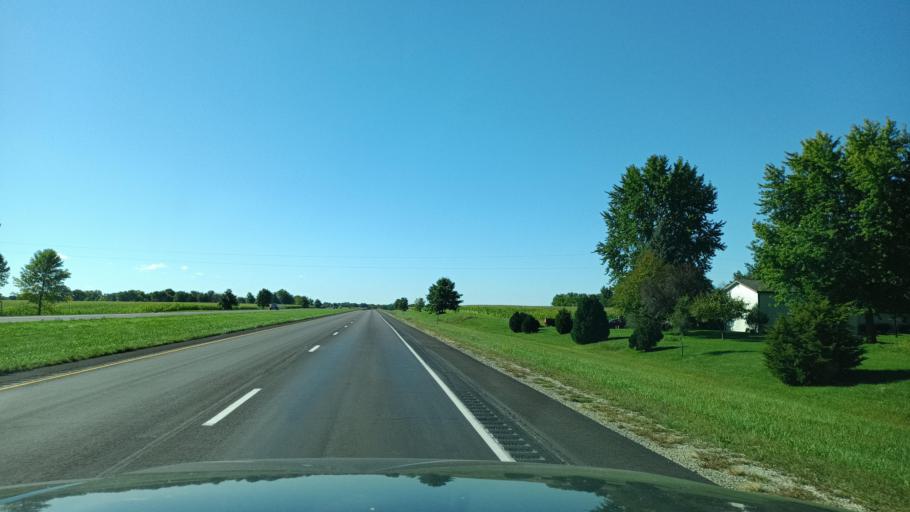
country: US
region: Iowa
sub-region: Lee County
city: Keokuk
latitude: 40.4717
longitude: -91.4448
